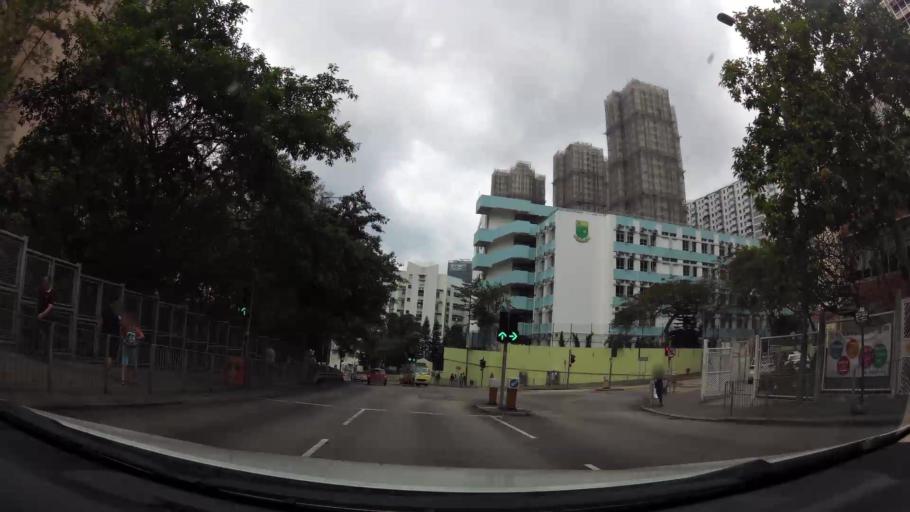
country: HK
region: Kowloon City
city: Kowloon
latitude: 22.3186
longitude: 114.2229
